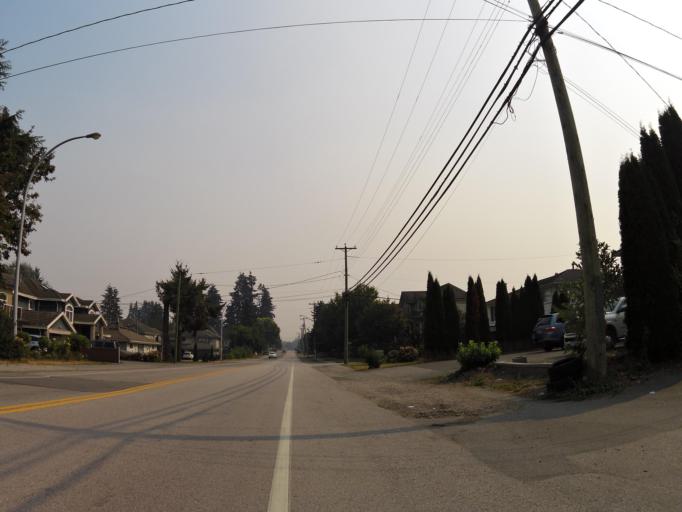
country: CA
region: British Columbia
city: Delta
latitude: 49.1559
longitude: -122.8875
